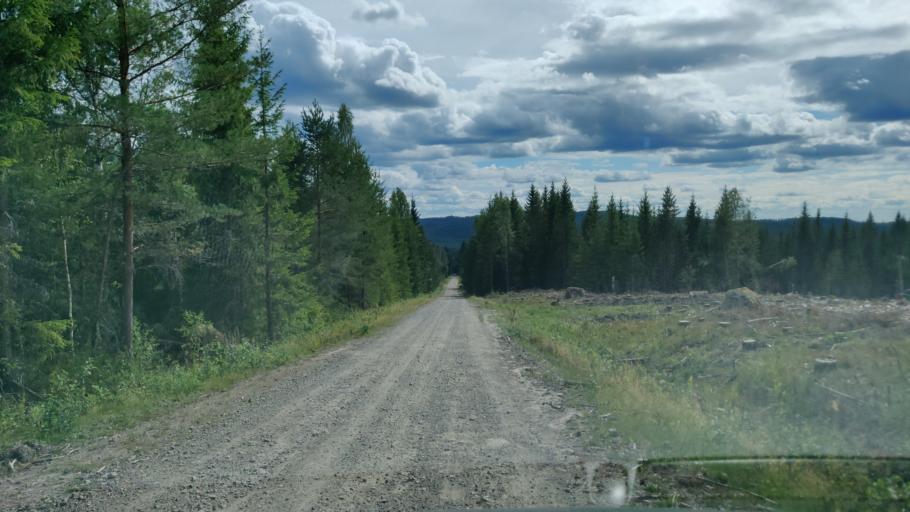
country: SE
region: Vaermland
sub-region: Hagfors Kommun
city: Hagfors
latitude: 60.0107
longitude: 13.7276
